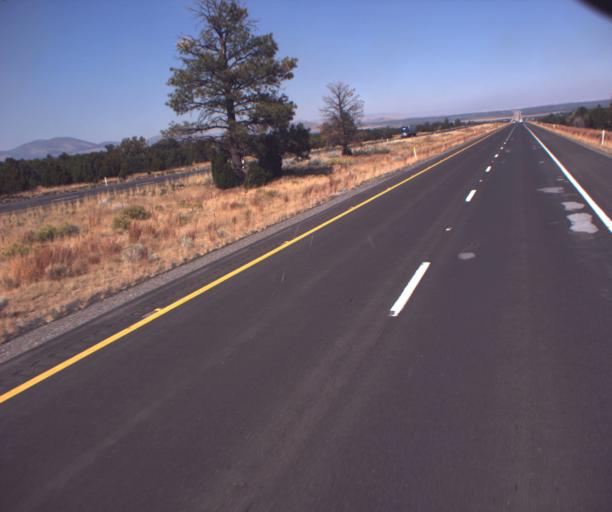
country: US
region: Arizona
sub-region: Coconino County
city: Flagstaff
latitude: 35.4000
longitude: -111.5760
